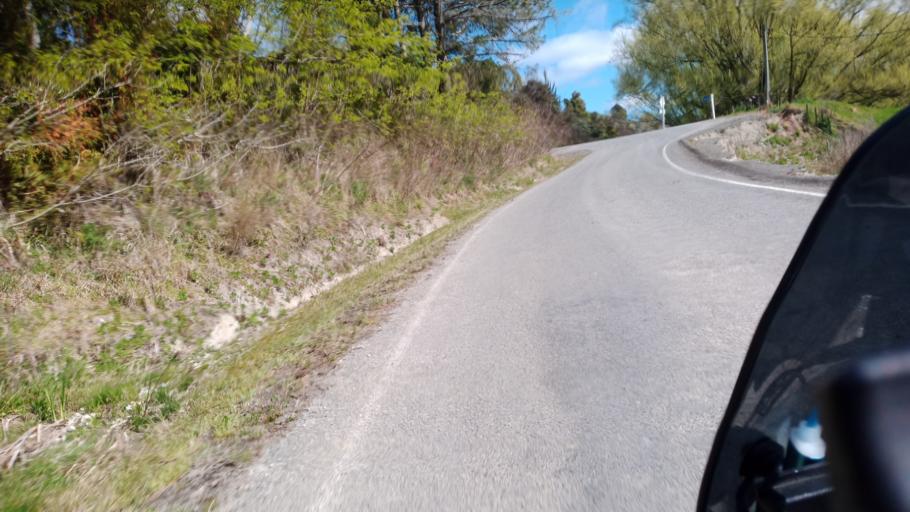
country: NZ
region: Gisborne
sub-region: Gisborne District
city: Gisborne
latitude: -38.7875
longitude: 177.7824
